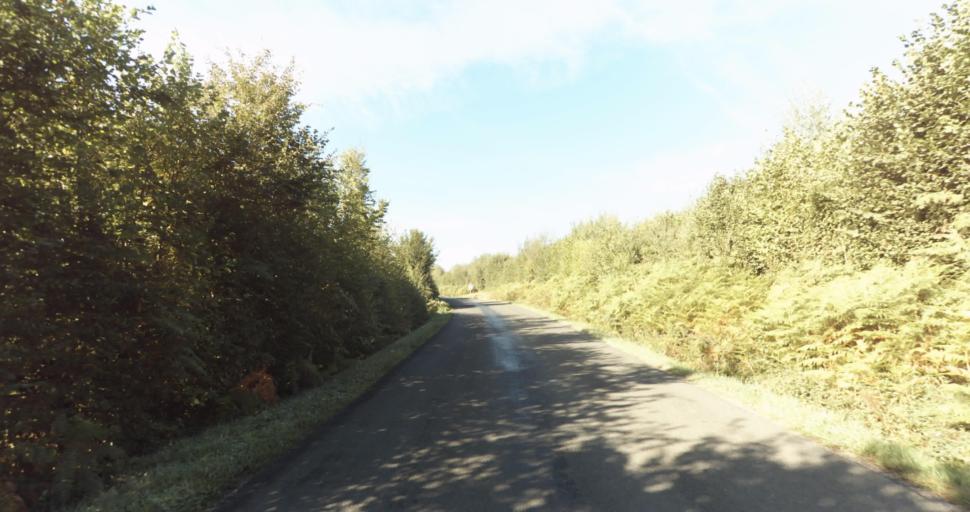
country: FR
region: Lower Normandy
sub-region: Departement de l'Orne
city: Vimoutiers
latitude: 48.9264
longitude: 0.2520
